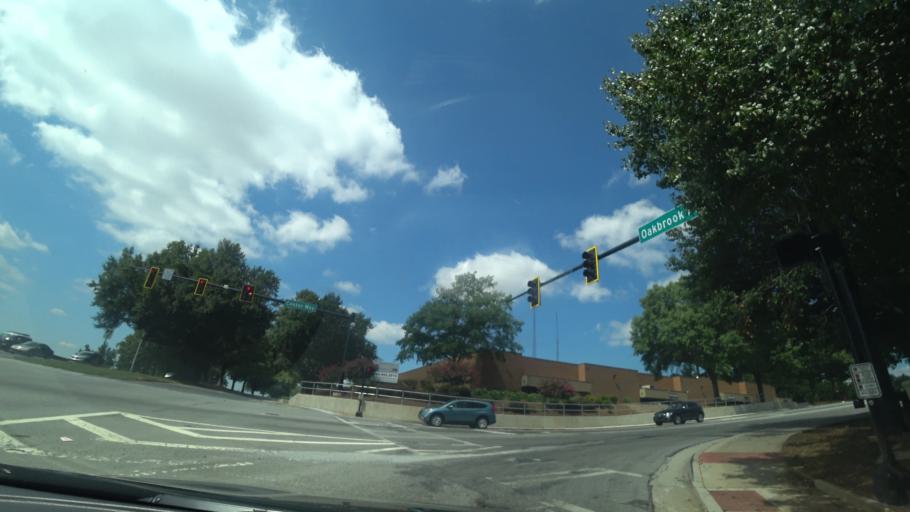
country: US
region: Georgia
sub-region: Gwinnett County
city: Norcross
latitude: 33.9165
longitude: -84.1959
